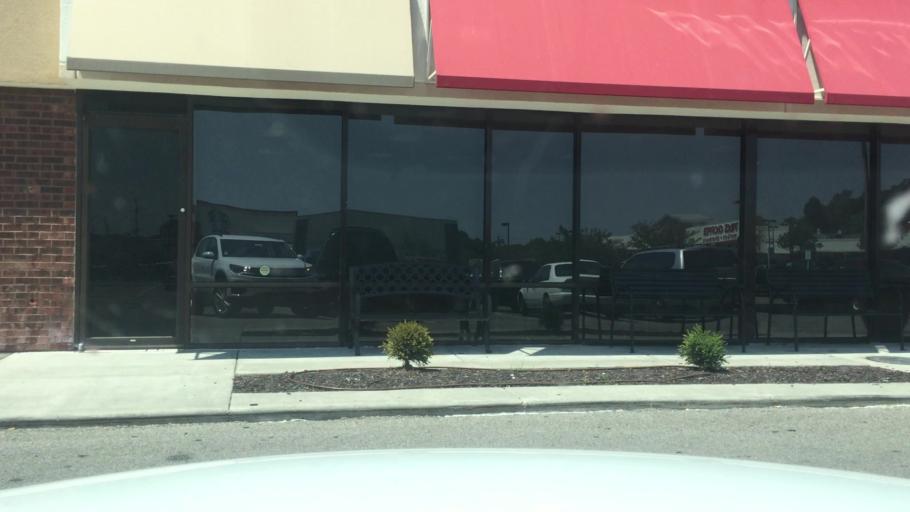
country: US
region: Kansas
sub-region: Johnson County
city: Shawnee
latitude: 39.0152
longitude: -94.7280
